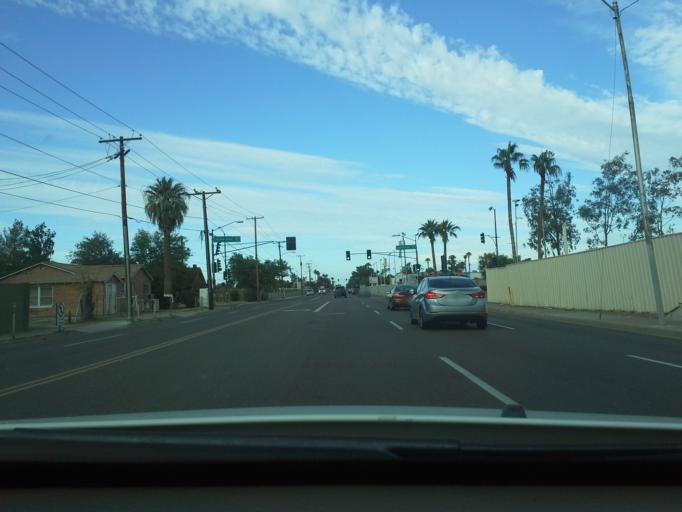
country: US
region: Arizona
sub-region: Maricopa County
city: Phoenix
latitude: 33.4702
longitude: -112.0999
